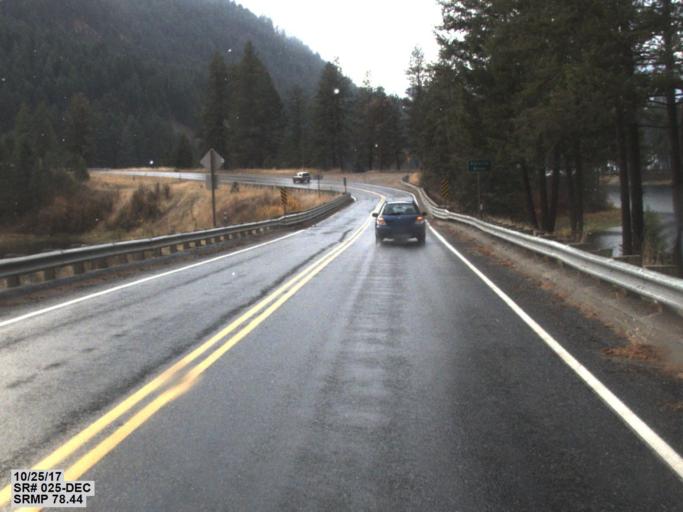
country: US
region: Washington
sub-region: Stevens County
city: Kettle Falls
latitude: 48.5734
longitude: -118.0865
